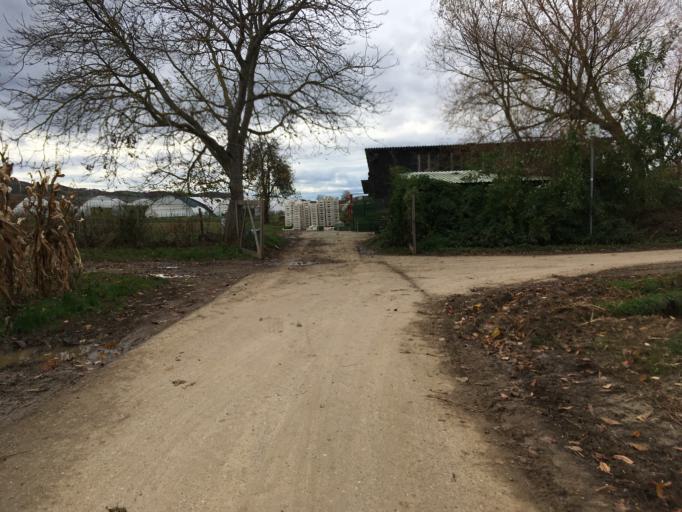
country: DE
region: Baden-Wuerttemberg
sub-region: Freiburg Region
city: Endingen
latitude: 48.1459
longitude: 7.6761
